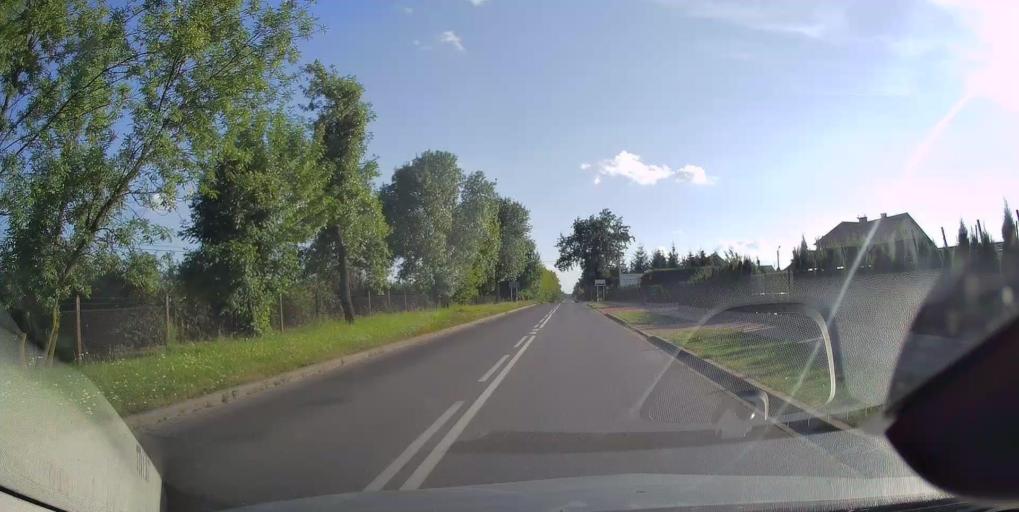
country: PL
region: Masovian Voivodeship
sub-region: Powiat grojecki
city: Belsk Duzy
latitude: 51.8318
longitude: 20.8172
